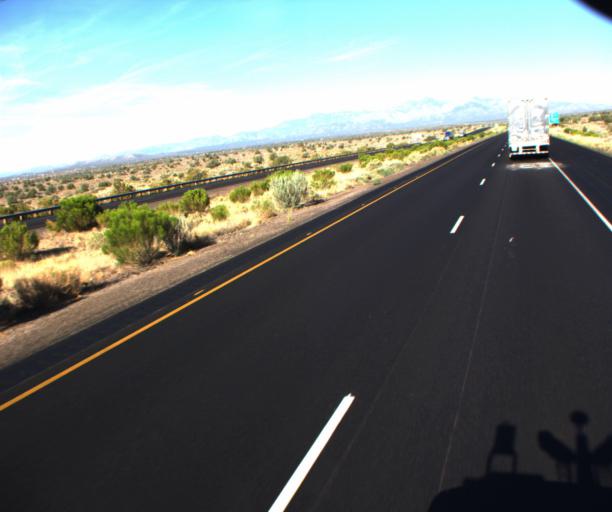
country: US
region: Arizona
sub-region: Mohave County
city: New Kingman-Butler
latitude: 35.1614
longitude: -113.6758
